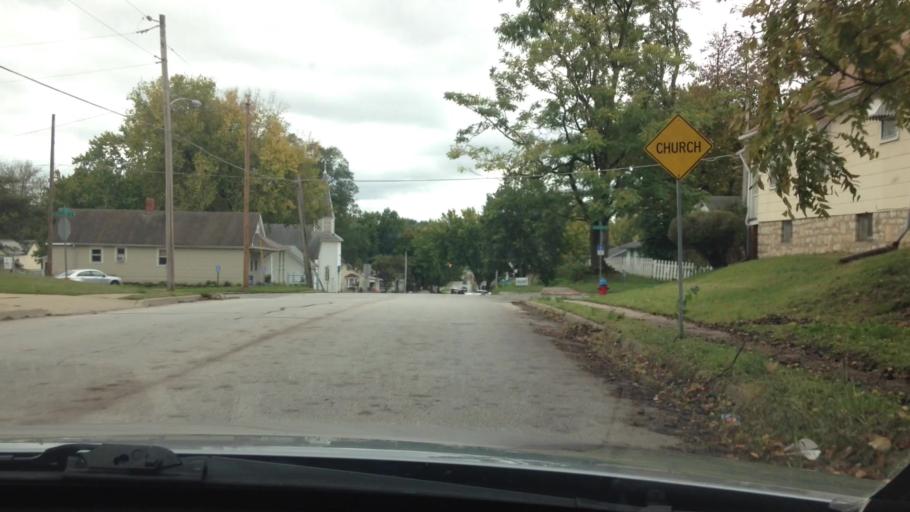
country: US
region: Kansas
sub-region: Leavenworth County
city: Leavenworth
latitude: 39.3235
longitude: -94.9283
